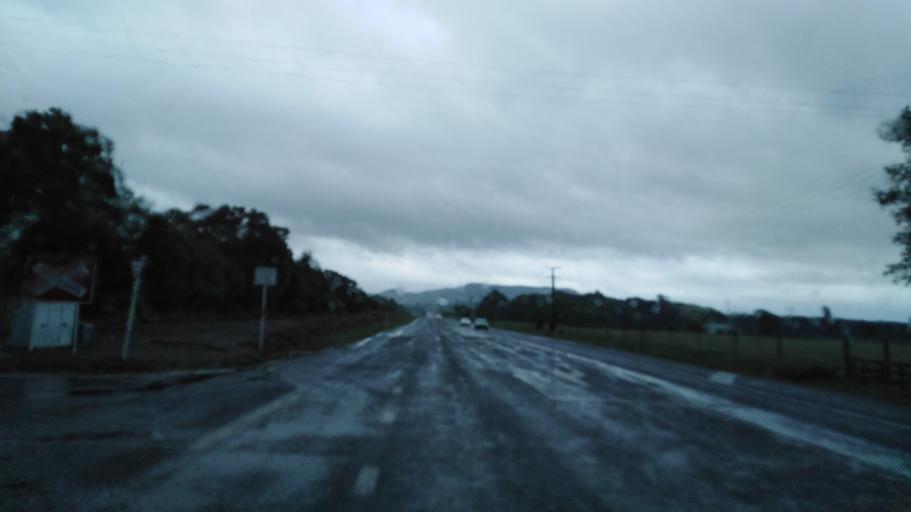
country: NZ
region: Wellington
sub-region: Kapiti Coast District
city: Otaki
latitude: -40.7049
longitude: 175.2207
